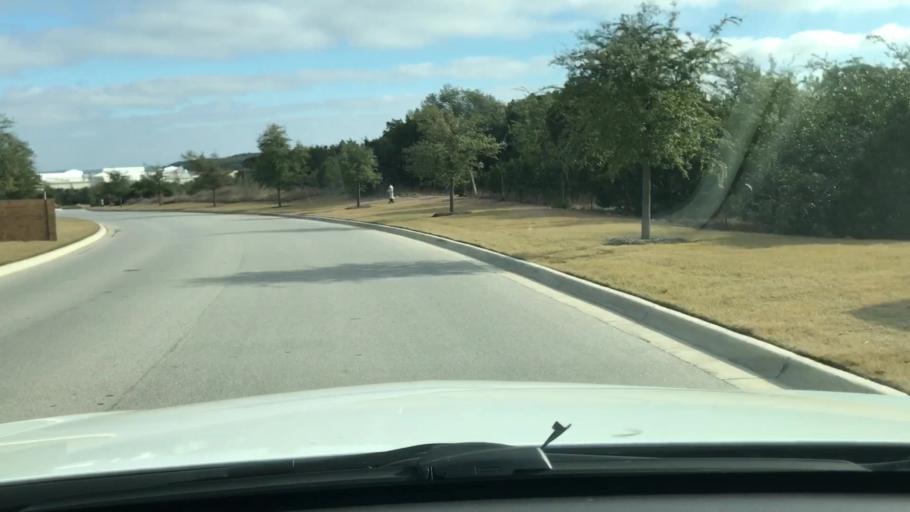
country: US
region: Texas
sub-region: Travis County
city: Bee Cave
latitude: 30.3157
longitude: -97.9589
